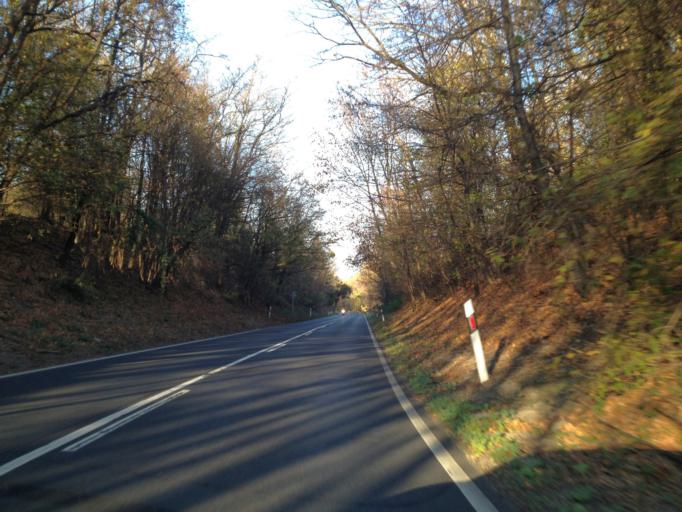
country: HU
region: Veszprem
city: Zirc
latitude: 47.3418
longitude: 17.8782
